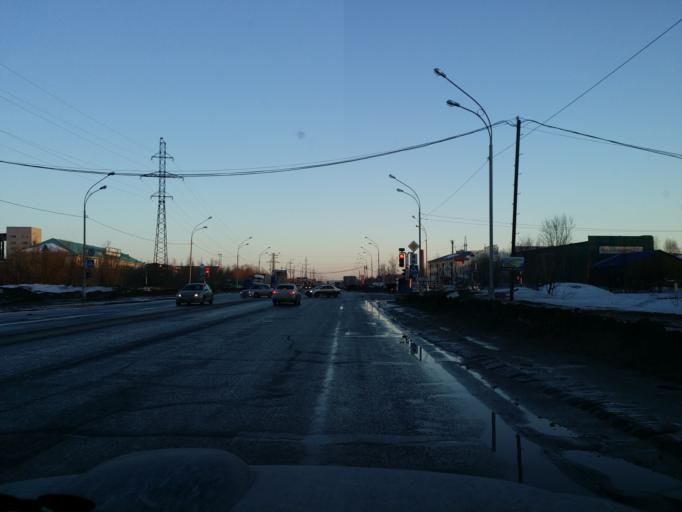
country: RU
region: Khanty-Mansiyskiy Avtonomnyy Okrug
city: Nizhnevartovsk
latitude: 60.9561
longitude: 76.5298
